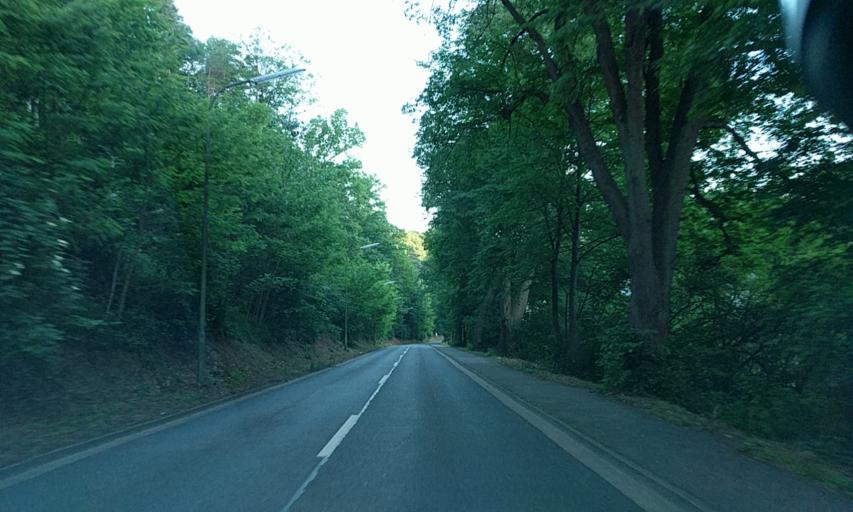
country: DE
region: Rheinland-Pfalz
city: Otterbach
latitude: 49.4640
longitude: 7.7616
